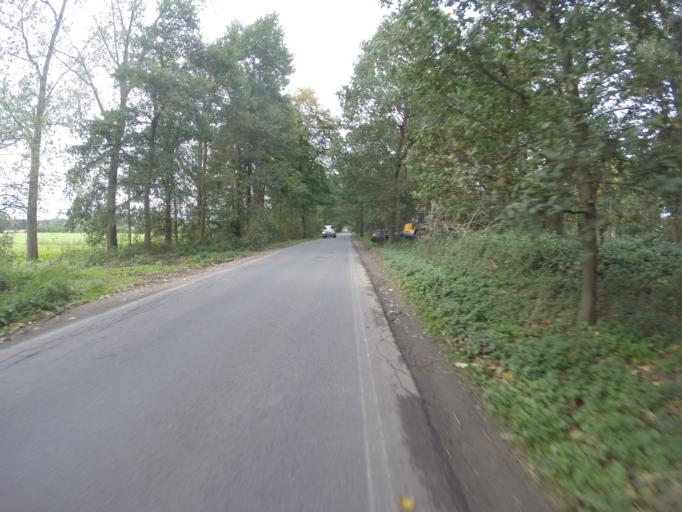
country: BE
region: Flanders
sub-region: Provincie Oost-Vlaanderen
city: Knesselare
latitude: 51.1046
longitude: 3.4060
